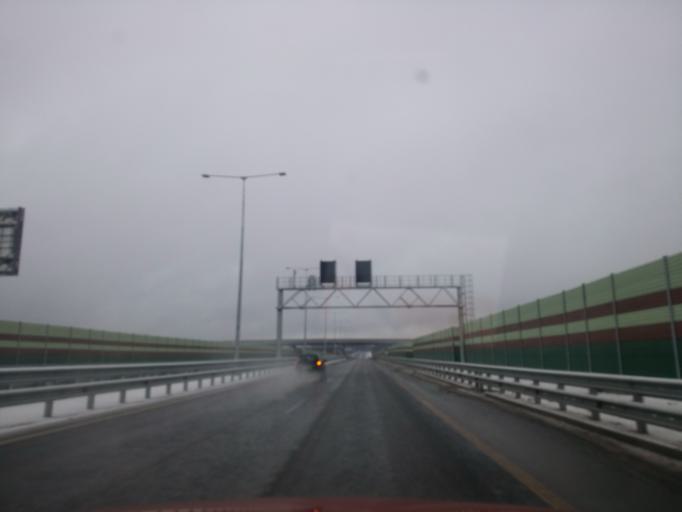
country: RU
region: Tverskaya
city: Likhoslavl'
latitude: 56.9788
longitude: 35.4321
